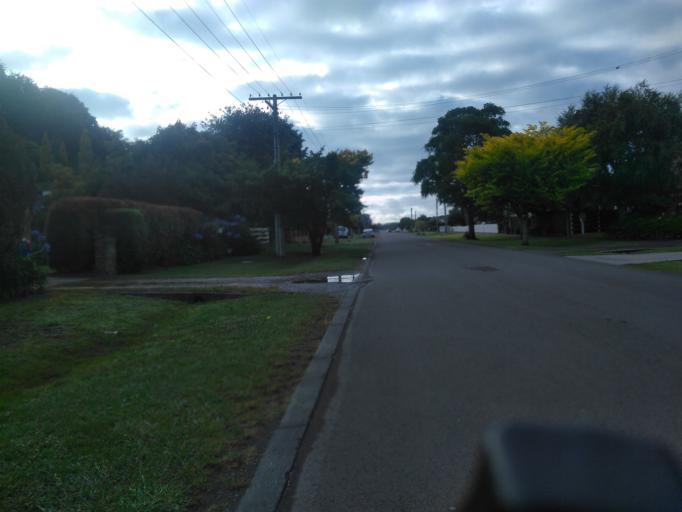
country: NZ
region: Gisborne
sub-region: Gisborne District
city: Gisborne
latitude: -38.6508
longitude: 178.0229
